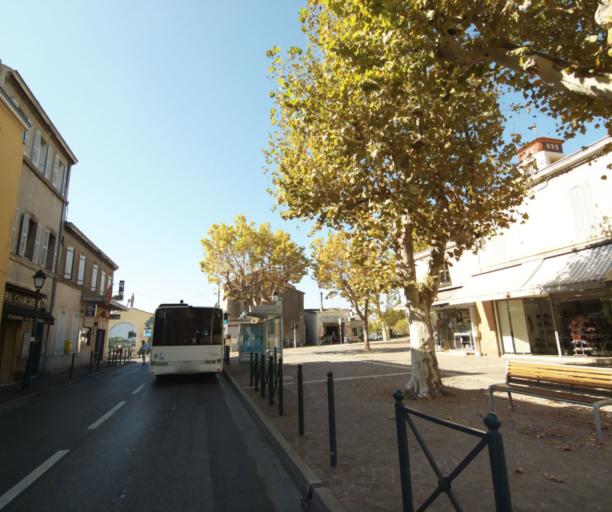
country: FR
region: Provence-Alpes-Cote d'Azur
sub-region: Departement des Bouches-du-Rhone
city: Plan-de-Cuques
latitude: 43.3477
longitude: 5.4640
